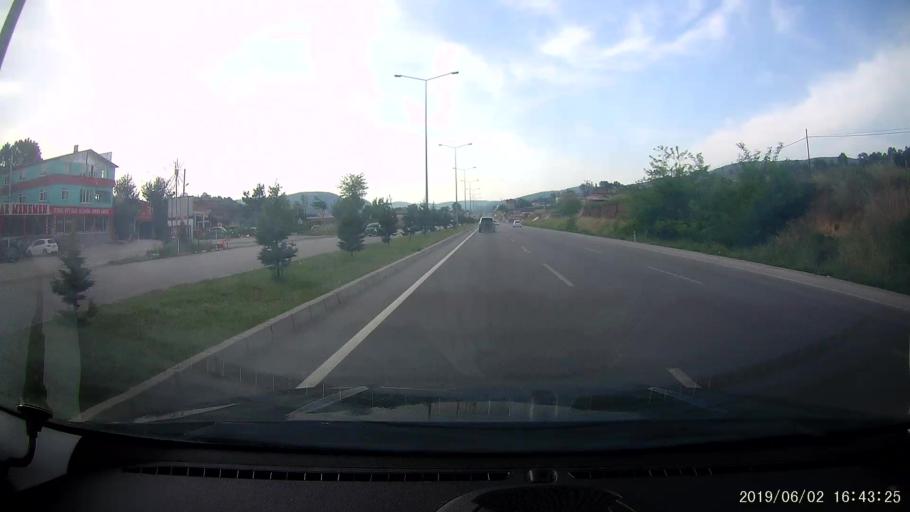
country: TR
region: Samsun
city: Kavak
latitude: 41.1349
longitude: 36.1275
